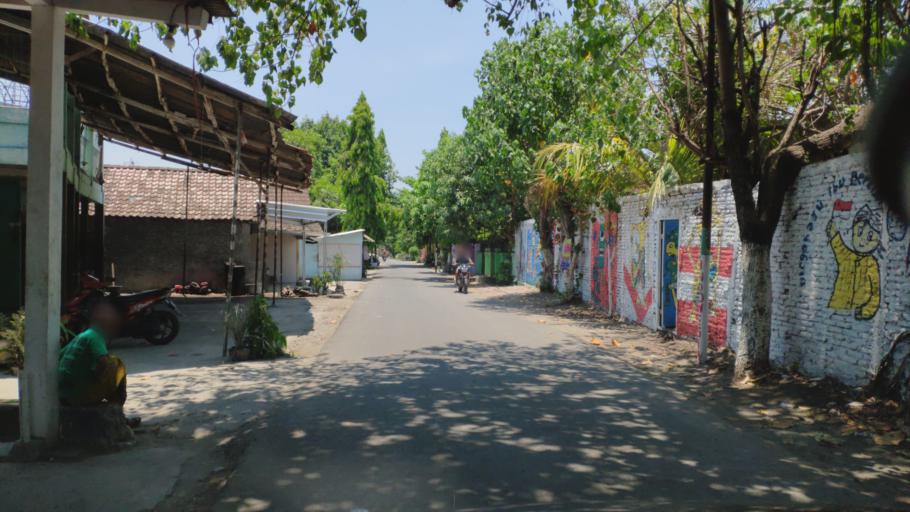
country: ID
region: Central Java
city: Tambakkromo
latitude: -7.1554
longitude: 111.5791
